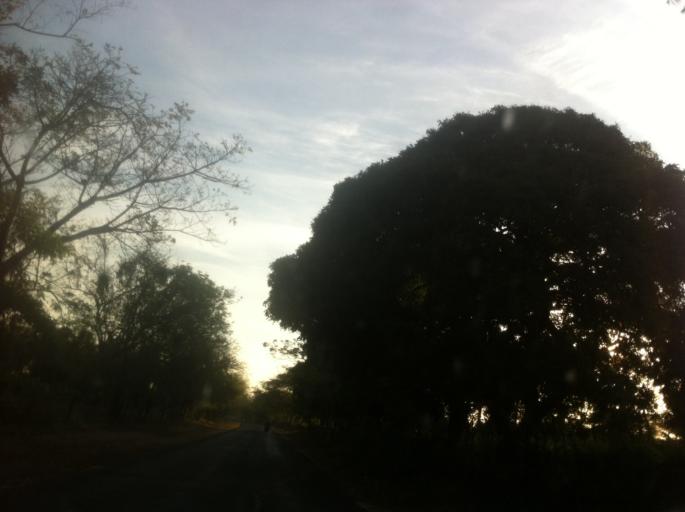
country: NI
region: Rivas
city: Potosi
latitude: 11.4958
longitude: -85.8656
